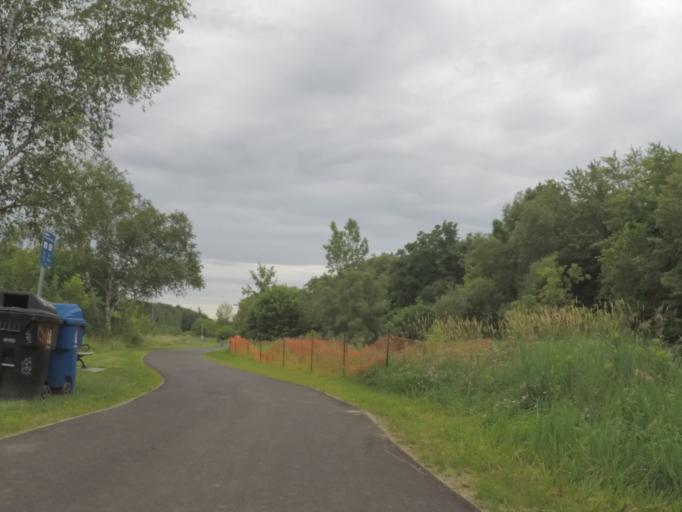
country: CA
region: Ontario
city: Etobicoke
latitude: 43.6704
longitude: -79.5689
